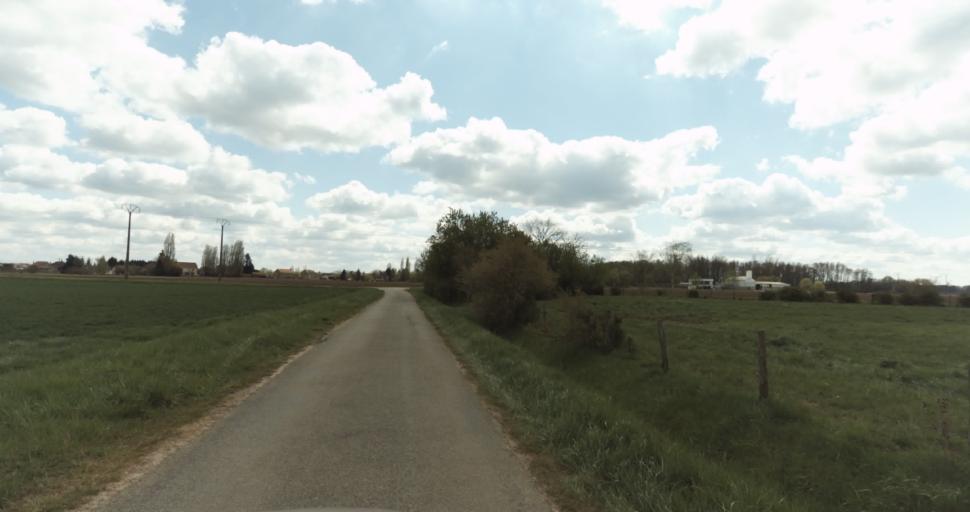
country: FR
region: Bourgogne
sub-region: Departement de la Cote-d'Or
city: Auxonne
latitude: 47.1873
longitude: 5.3795
